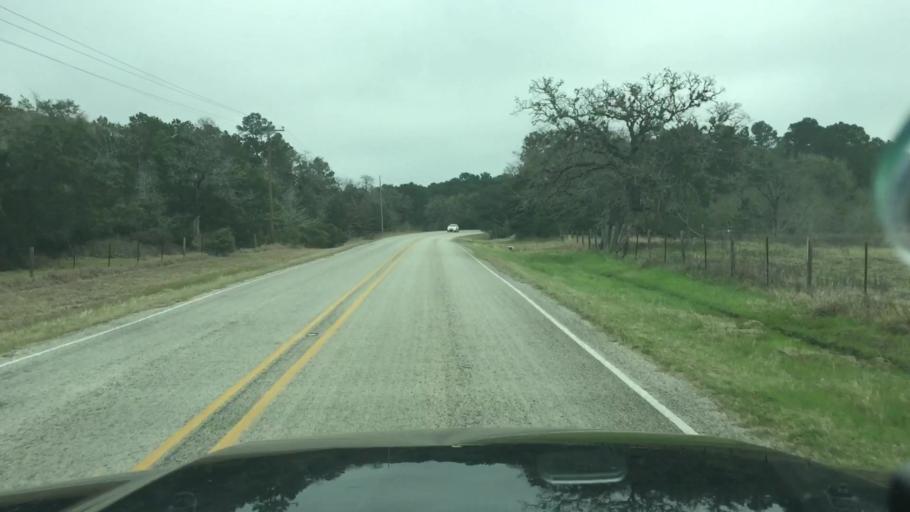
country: US
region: Texas
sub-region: Fayette County
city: La Grange
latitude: 30.0124
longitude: -96.9262
